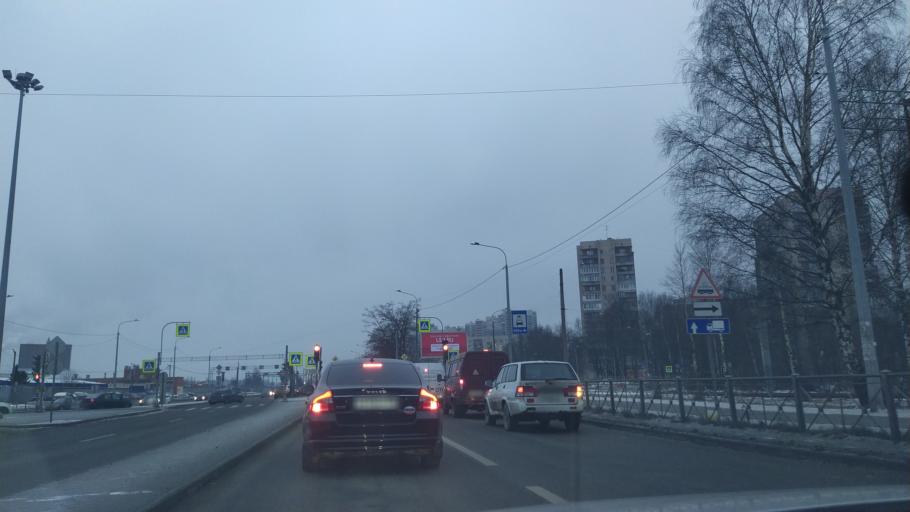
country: RU
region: Leningrad
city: Murino
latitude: 60.0402
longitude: 30.4323
